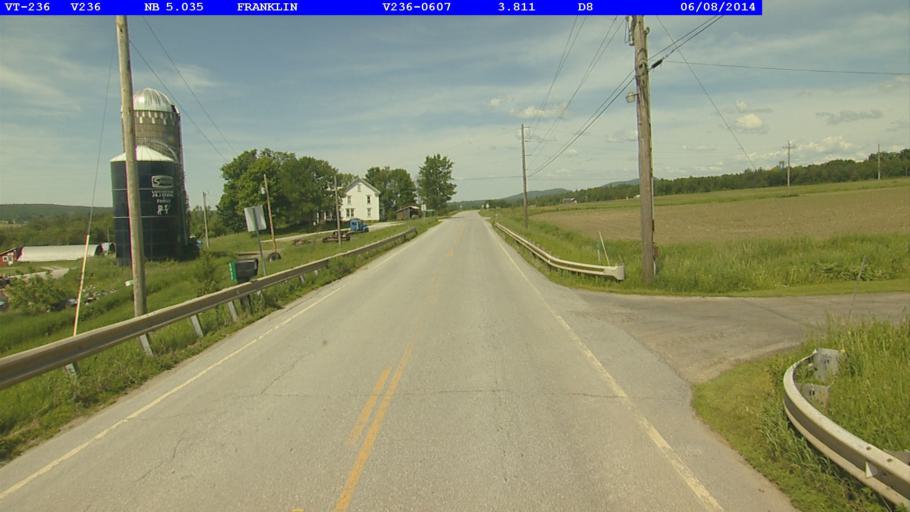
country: US
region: Vermont
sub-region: Franklin County
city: Enosburg Falls
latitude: 44.9797
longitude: -72.8439
